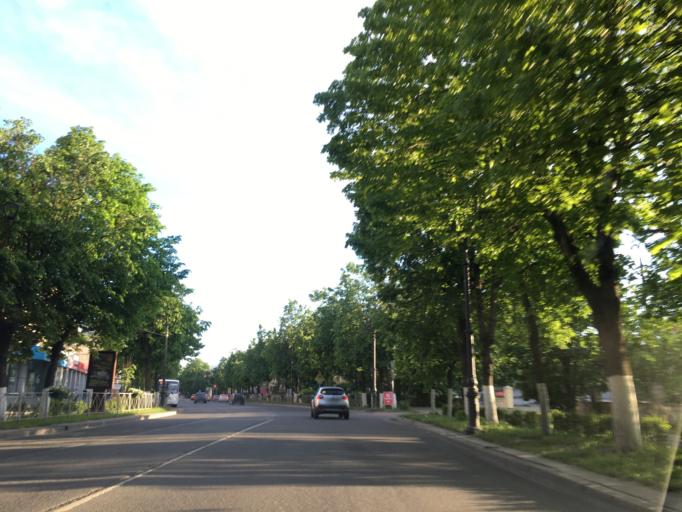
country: RU
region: Leningrad
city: Gatchina
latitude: 59.5741
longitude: 30.1274
